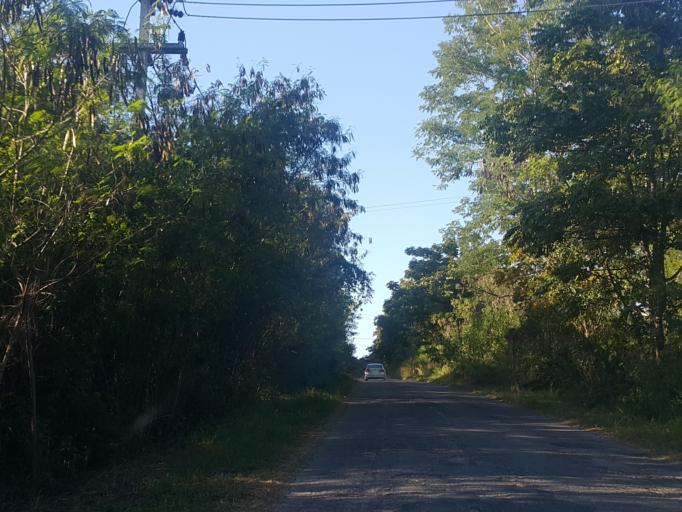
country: TH
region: Chiang Mai
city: San Sai
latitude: 18.9332
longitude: 99.1387
